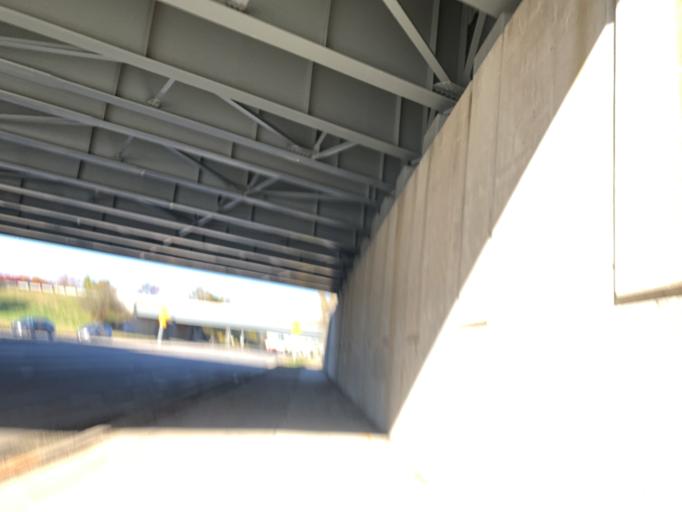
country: US
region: Kentucky
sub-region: Jefferson County
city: Shively
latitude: 38.1850
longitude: -85.8130
